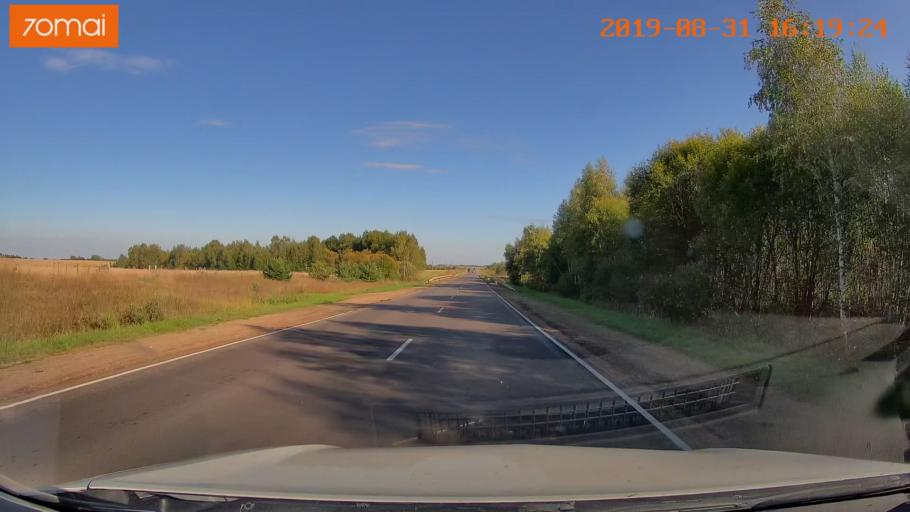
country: RU
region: Kaluga
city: Nikola-Lenivets
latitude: 54.5294
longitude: 35.5778
